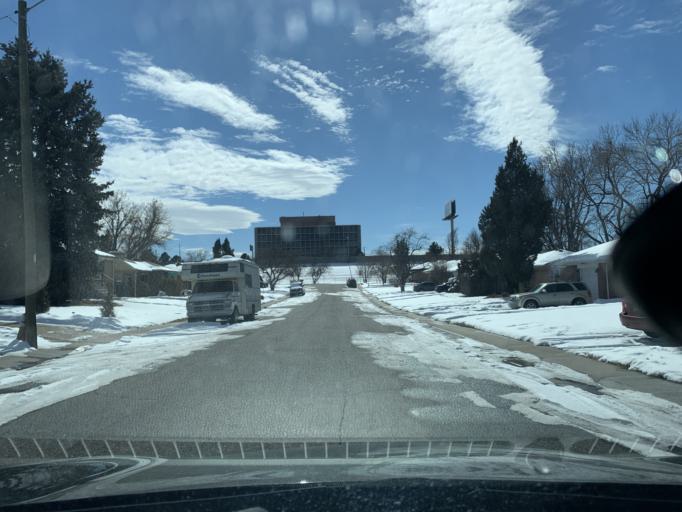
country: US
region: Colorado
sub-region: Jefferson County
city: Wheat Ridge
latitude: 39.7851
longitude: -105.0617
